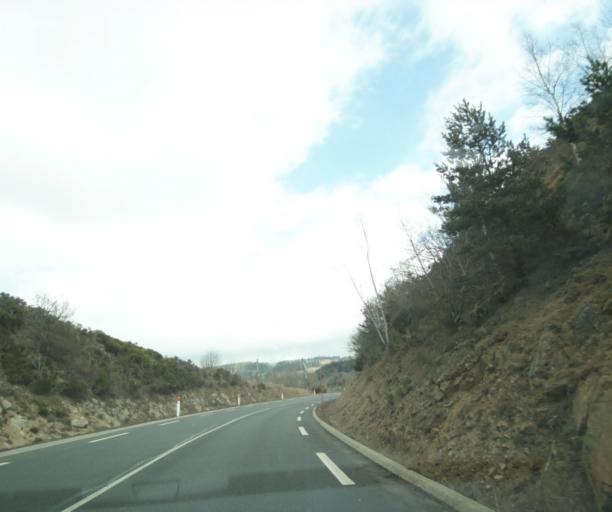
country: FR
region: Languedoc-Roussillon
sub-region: Departement de la Lozere
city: Mende
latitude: 44.5994
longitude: 3.6681
